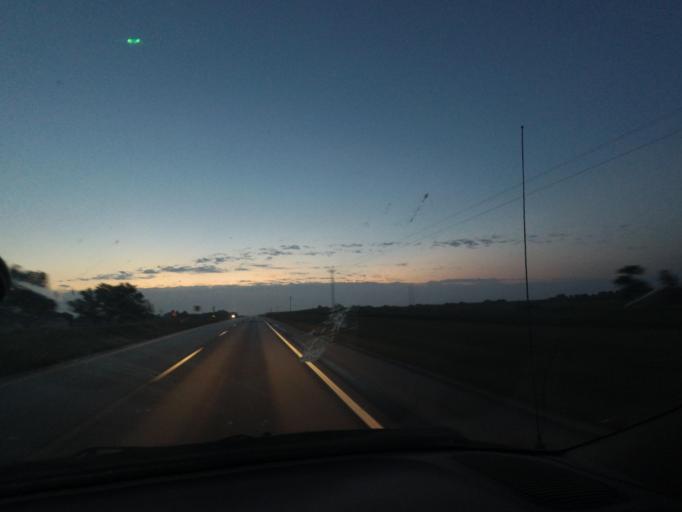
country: US
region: Missouri
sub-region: Linn County
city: Linneus
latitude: 39.7777
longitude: -93.2602
